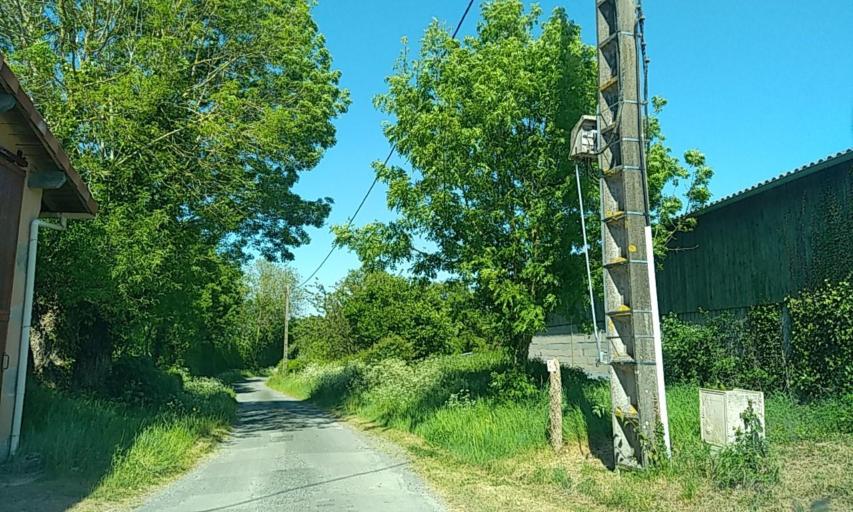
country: FR
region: Poitou-Charentes
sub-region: Departement des Deux-Sevres
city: Boisme
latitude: 46.7650
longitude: -0.4483
